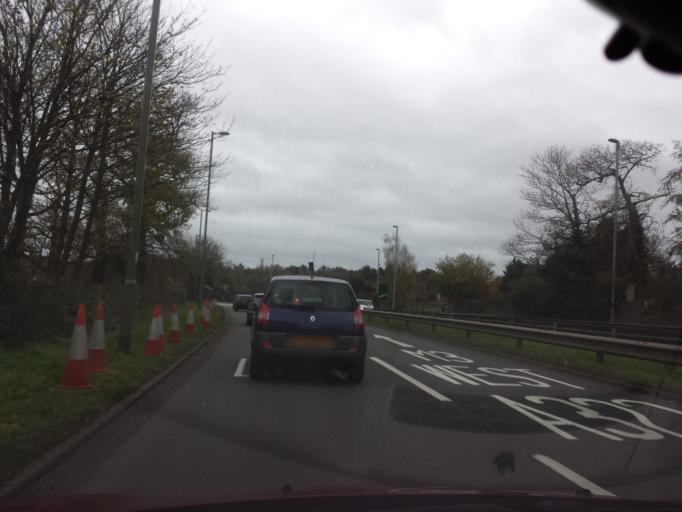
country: GB
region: England
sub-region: Surrey
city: Bagshot
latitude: 51.3575
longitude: -0.6828
